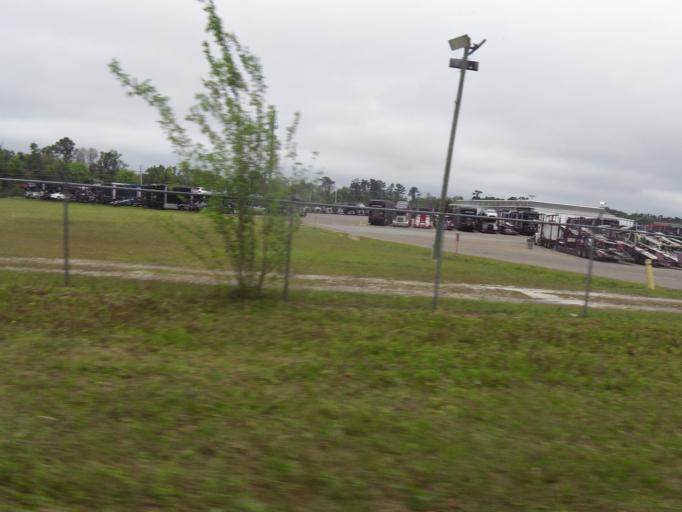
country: US
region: Florida
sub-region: Duval County
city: Jacksonville
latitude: 30.3675
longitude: -81.7252
